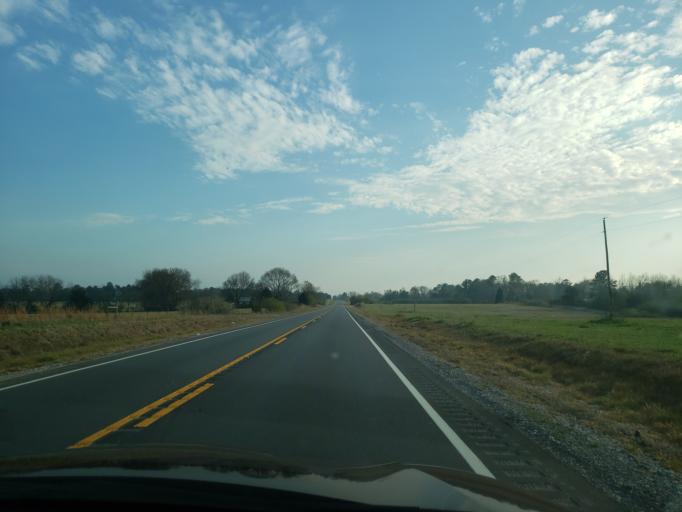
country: US
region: Alabama
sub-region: Hale County
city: Moundville
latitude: 32.8758
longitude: -87.6102
